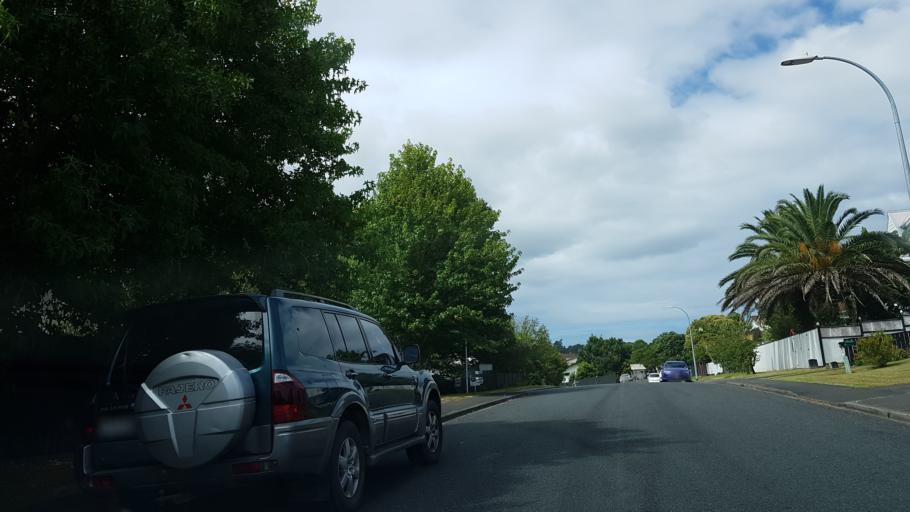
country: NZ
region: Auckland
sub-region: Auckland
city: North Shore
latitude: -36.7745
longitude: 174.7011
